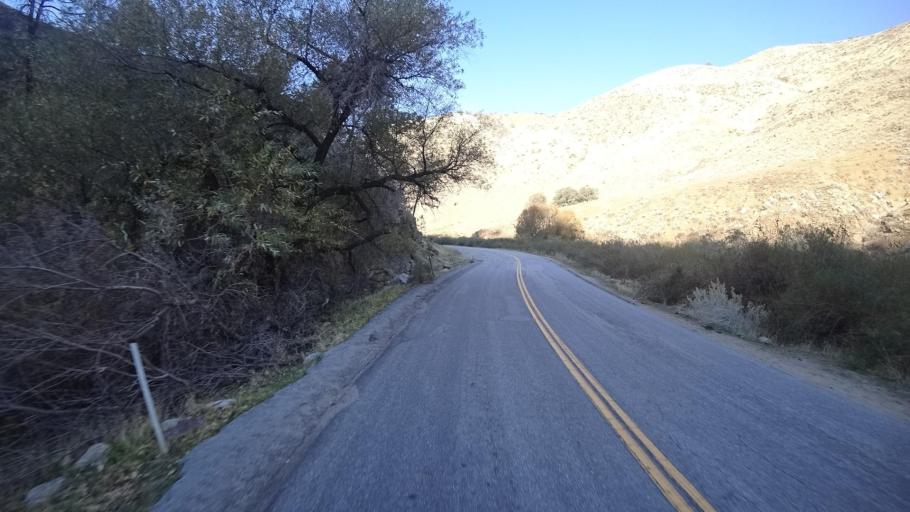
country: US
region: California
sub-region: Kern County
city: Bear Valley Springs
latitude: 35.3149
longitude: -118.5518
